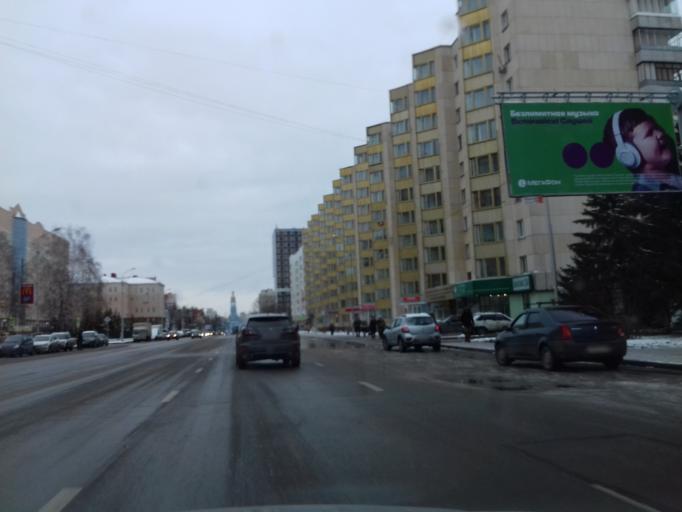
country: RU
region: Bashkortostan
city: Ufa
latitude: 54.7288
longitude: 55.9636
